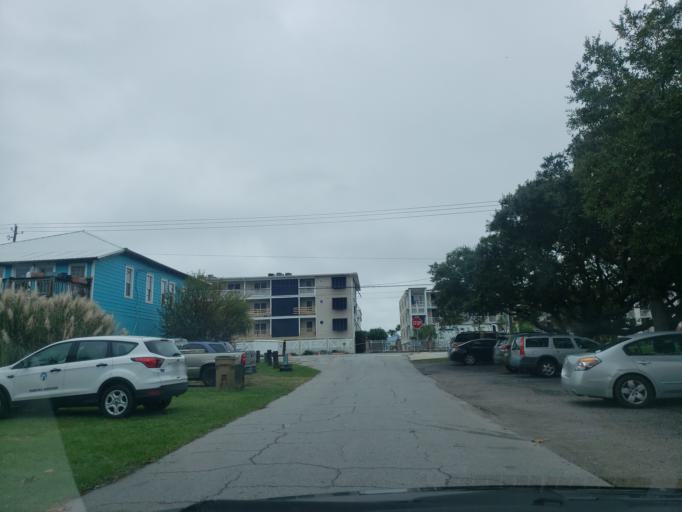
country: US
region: Georgia
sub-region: Chatham County
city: Tybee Island
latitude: 32.0091
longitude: -80.8432
